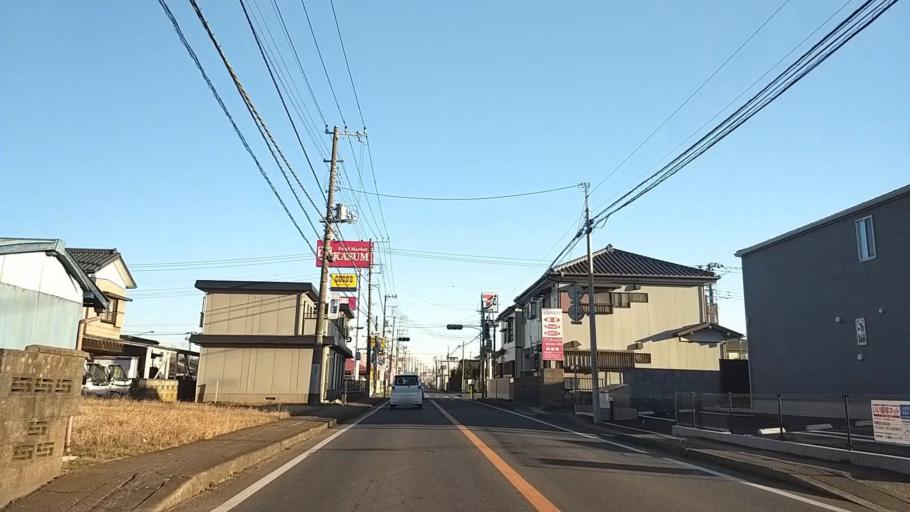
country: JP
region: Chiba
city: Hasaki
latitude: 35.7427
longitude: 140.7926
